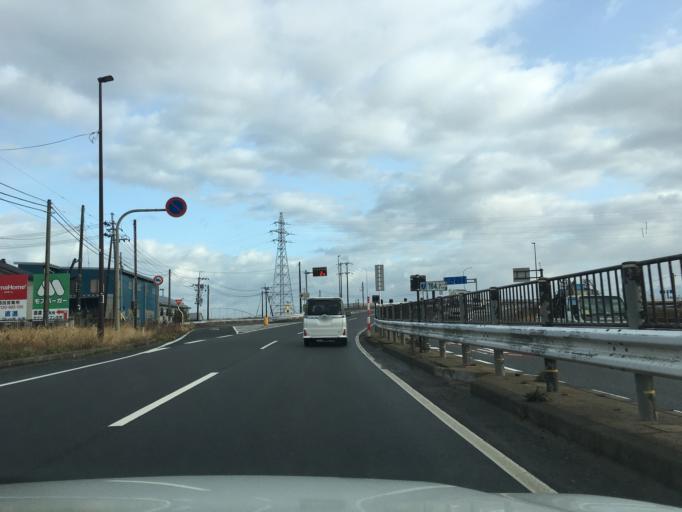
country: JP
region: Yamagata
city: Sakata
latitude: 38.8821
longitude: 139.8380
